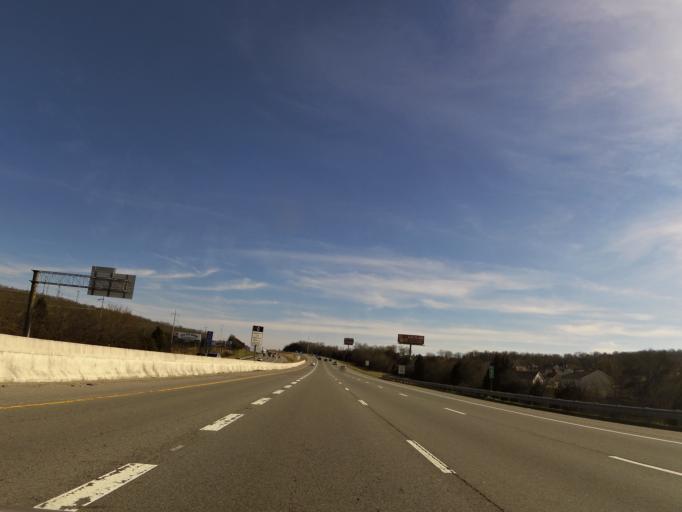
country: US
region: Tennessee
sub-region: Rutherford County
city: Smyrna
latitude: 35.9667
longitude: -86.5659
